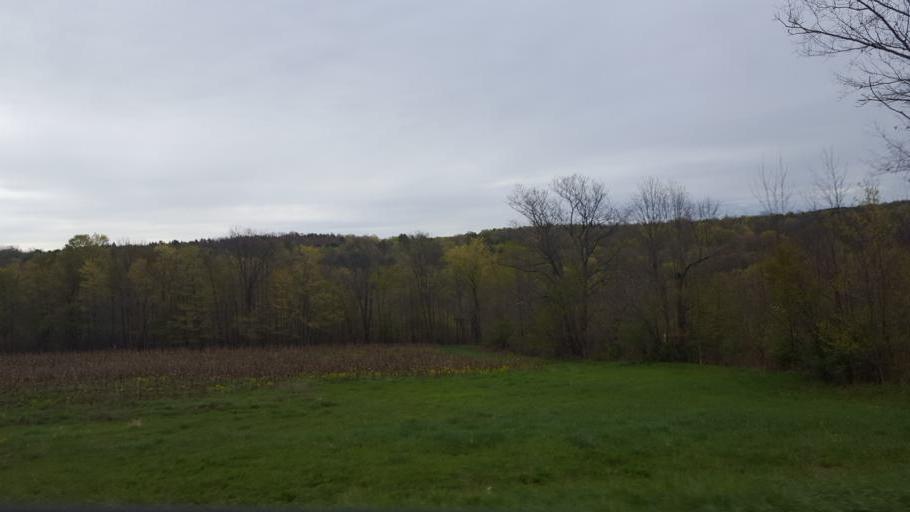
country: US
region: Pennsylvania
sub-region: Tioga County
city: Westfield
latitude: 42.0357
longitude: -77.4663
